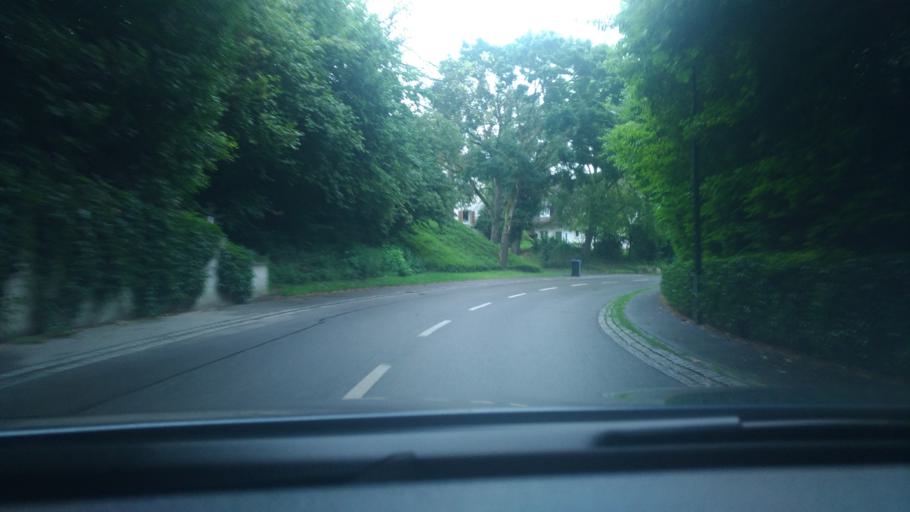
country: DE
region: Baden-Wuerttemberg
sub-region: Tuebingen Region
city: Sipplingen
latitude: 47.8318
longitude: 9.0957
